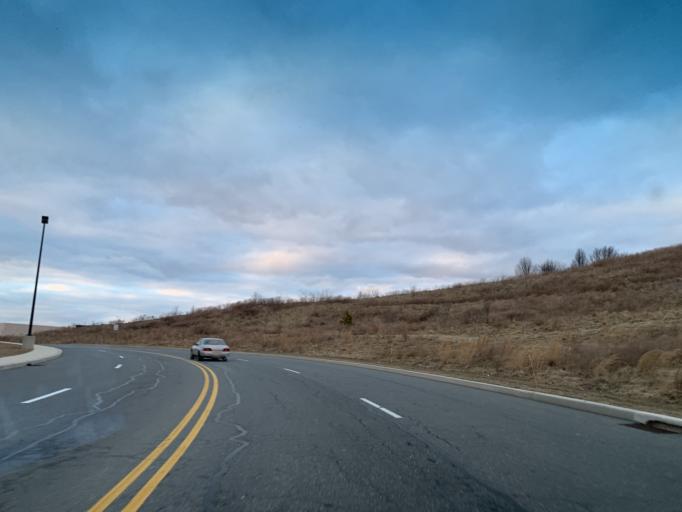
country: US
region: Delaware
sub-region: New Castle County
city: Bear
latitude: 39.6741
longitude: -75.6477
